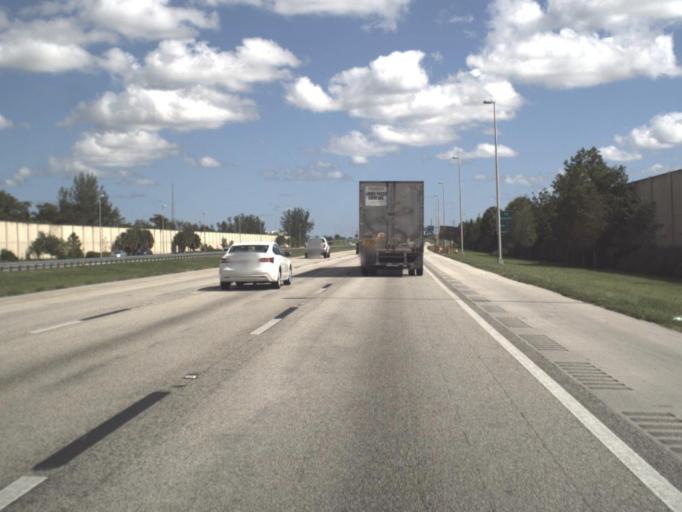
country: US
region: Florida
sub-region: Broward County
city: Parkland
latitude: 26.3003
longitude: -80.2139
